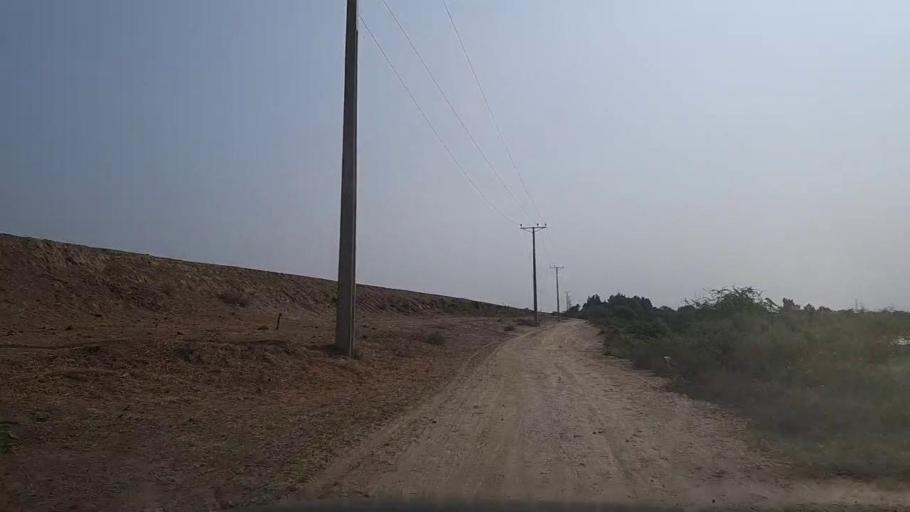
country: PK
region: Sindh
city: Chuhar Jamali
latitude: 24.5556
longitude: 67.9164
